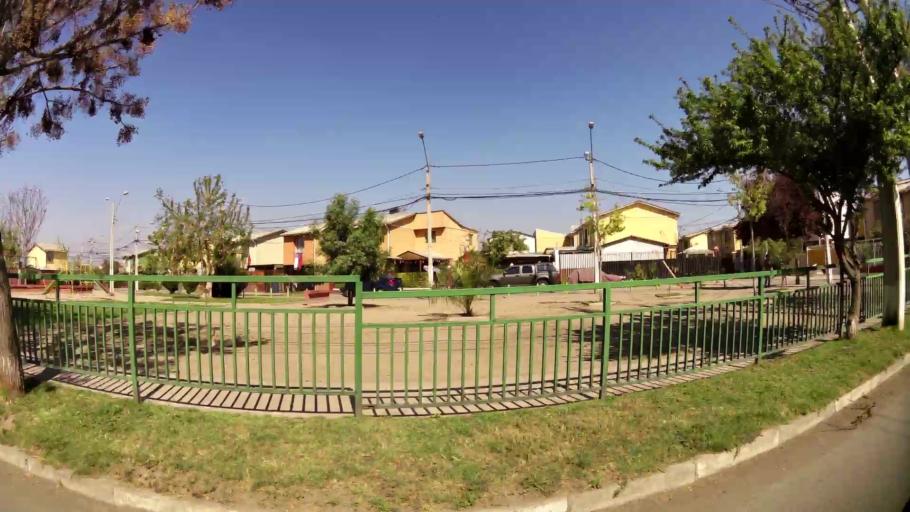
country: CL
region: Santiago Metropolitan
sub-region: Provincia de Santiago
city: Lo Prado
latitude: -33.3499
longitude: -70.7446
